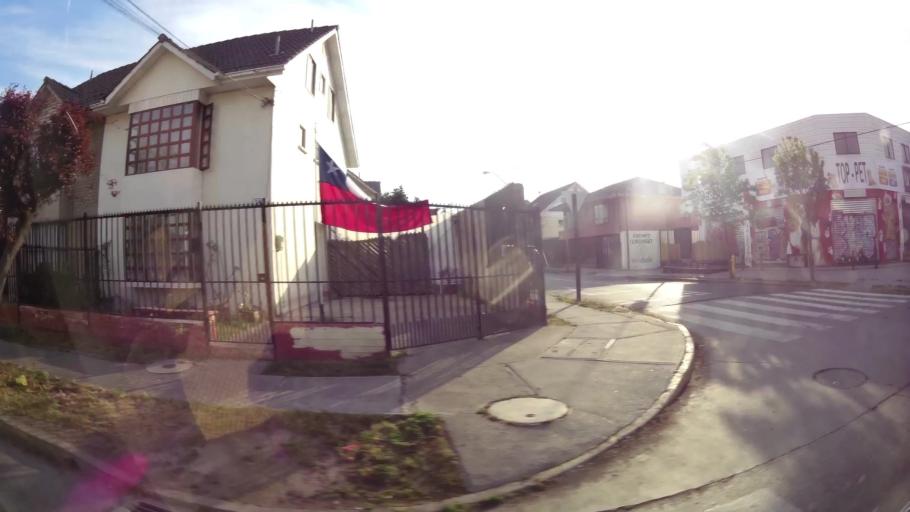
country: CL
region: Santiago Metropolitan
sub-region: Provincia de Talagante
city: Penaflor
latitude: -33.5560
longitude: -70.7925
